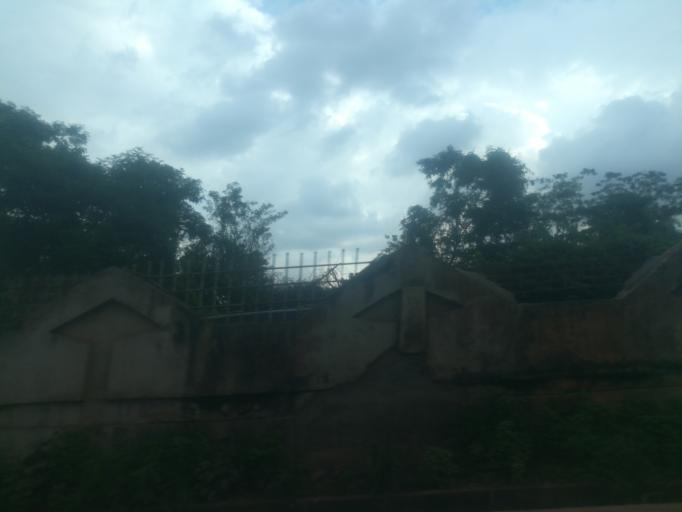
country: NG
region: Oyo
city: Ibadan
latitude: 7.4335
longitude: 3.9033
